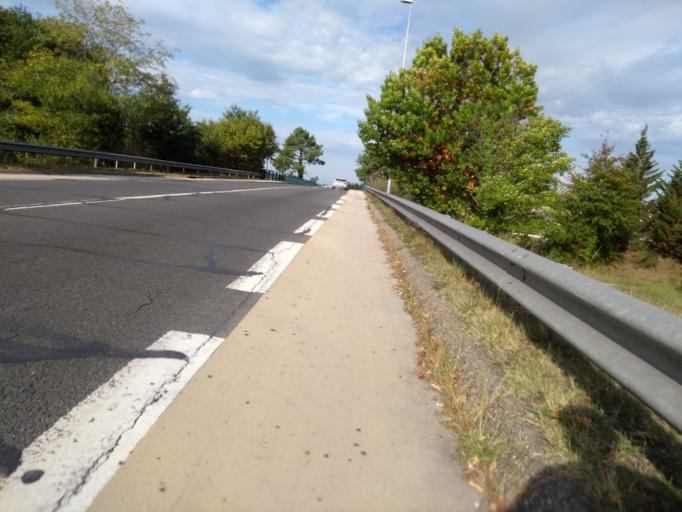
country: FR
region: Aquitaine
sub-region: Departement de la Gironde
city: Canejan
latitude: 44.7833
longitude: -0.6303
